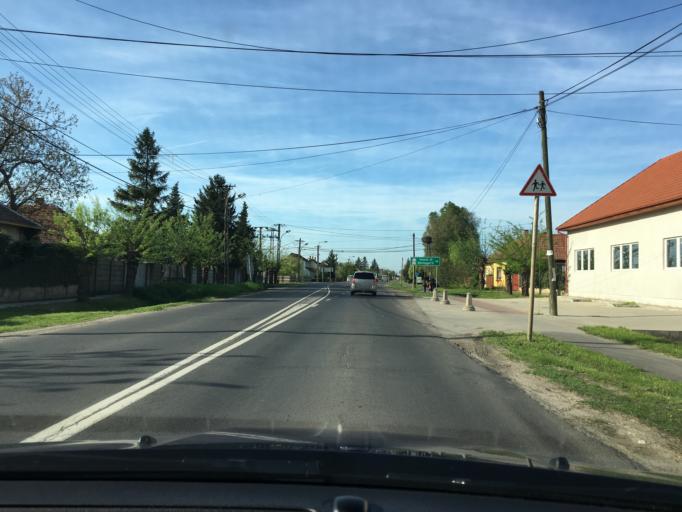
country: HU
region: Bekes
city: Mezobereny
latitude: 46.8338
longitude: 21.0276
